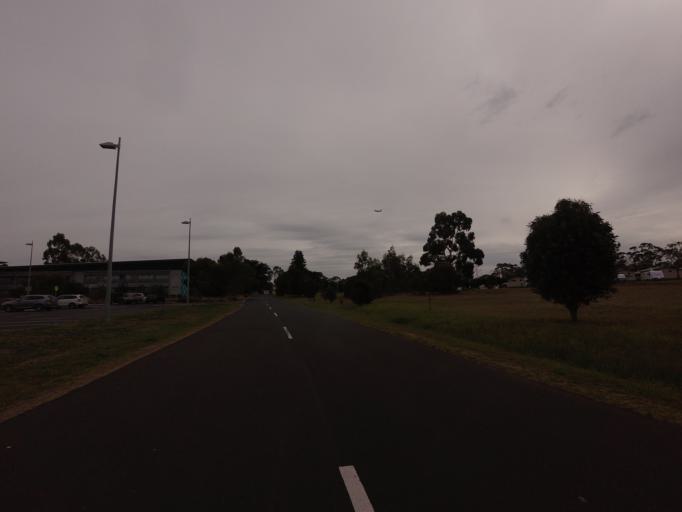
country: AU
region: Tasmania
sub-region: Clarence
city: Seven Mile Beach
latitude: -42.8322
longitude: 147.4922
